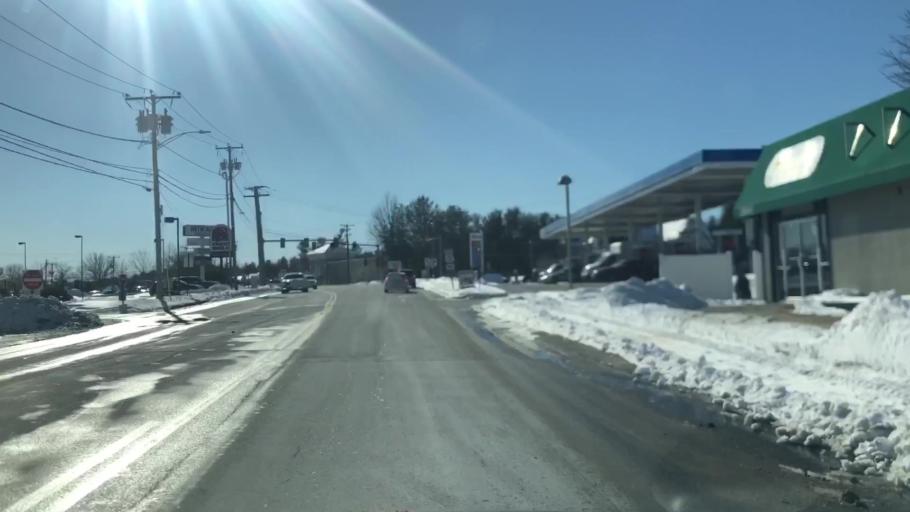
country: US
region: New Hampshire
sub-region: Hillsborough County
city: Pinardville
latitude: 42.9669
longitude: -71.4807
